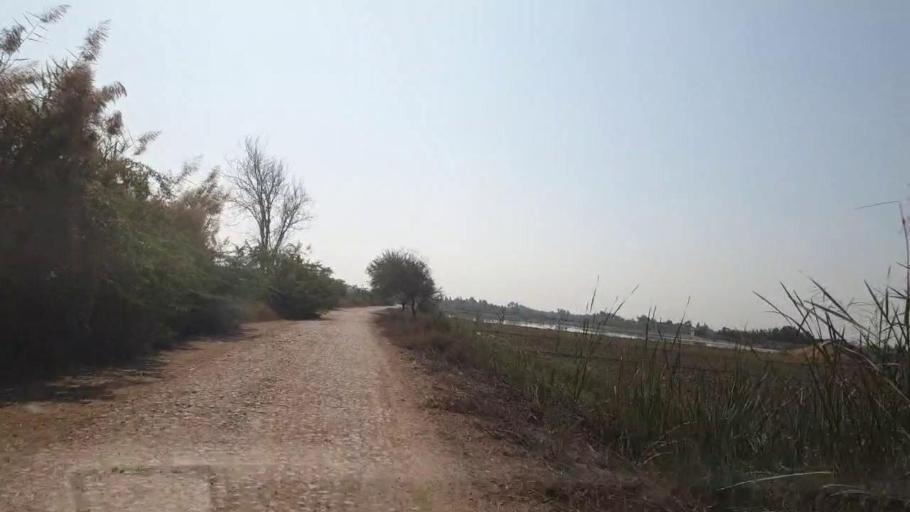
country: PK
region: Sindh
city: Gharo
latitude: 24.6837
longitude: 67.7494
